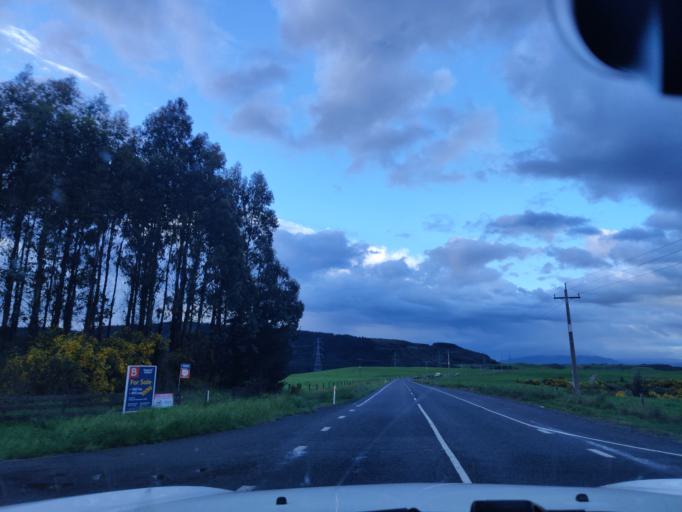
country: NZ
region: Waikato
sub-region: South Waikato District
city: Tokoroa
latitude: -38.3648
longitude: 175.8063
